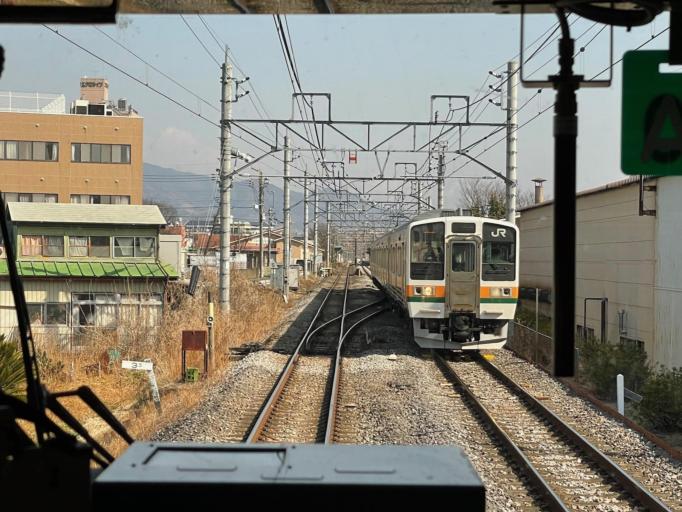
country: JP
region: Gunma
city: Shibukawa
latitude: 36.4866
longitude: 139.0071
